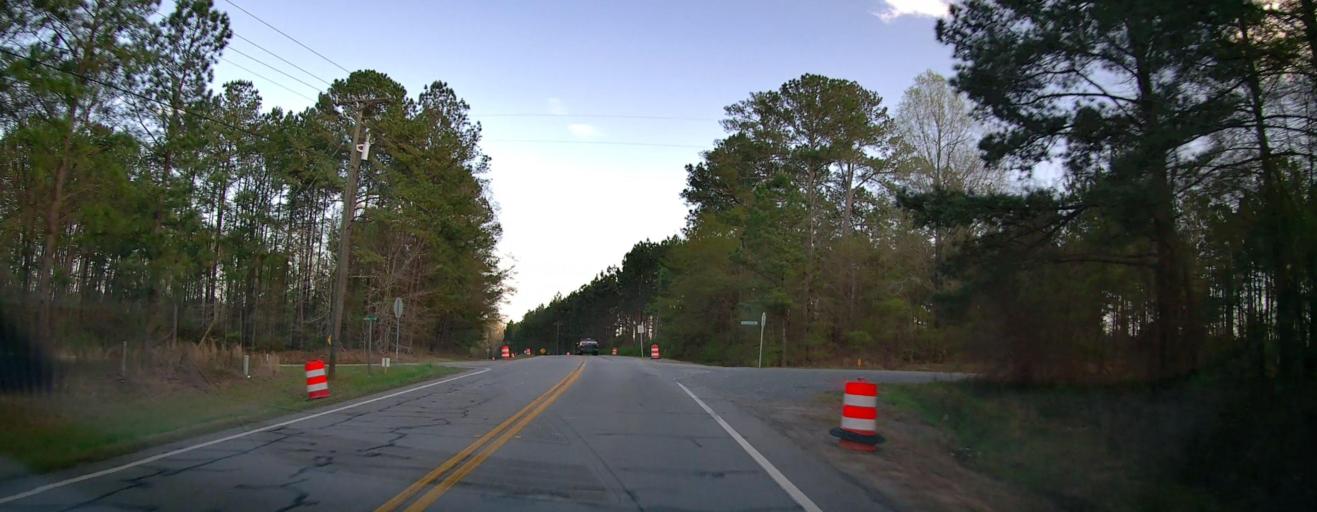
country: US
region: Georgia
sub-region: Putnam County
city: Eatonton
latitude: 33.1774
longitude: -83.4051
